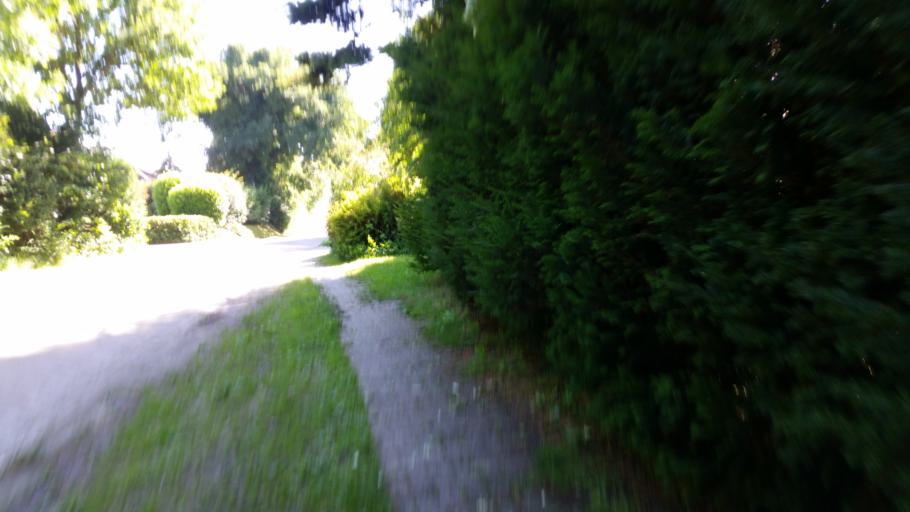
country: DE
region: Lower Saxony
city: Aurich
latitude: 53.4772
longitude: 7.4654
